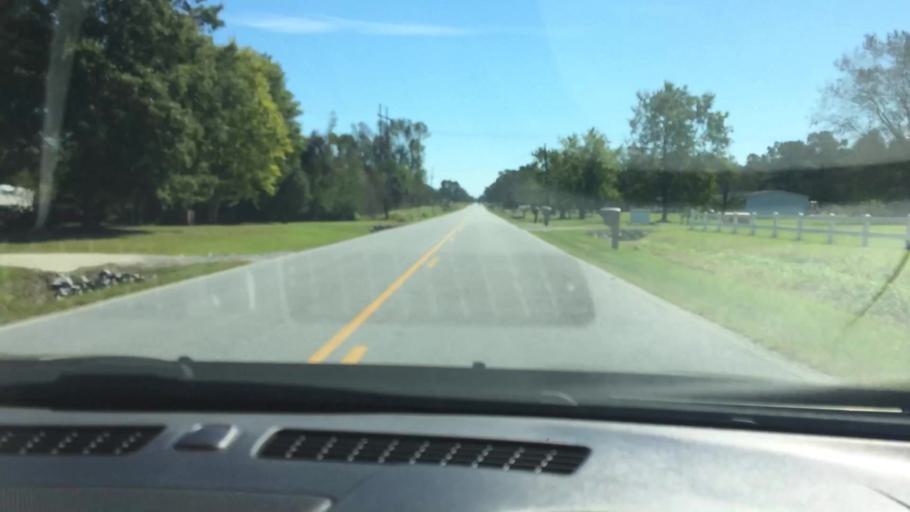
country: US
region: North Carolina
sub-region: Pitt County
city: Grifton
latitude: 35.3924
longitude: -77.3908
